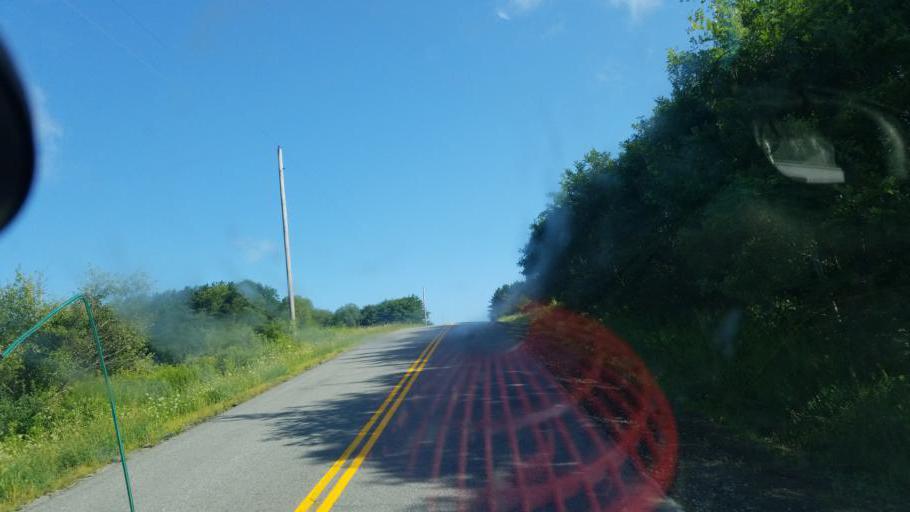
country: US
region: New York
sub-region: Allegany County
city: Andover
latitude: 42.1597
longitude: -77.7132
